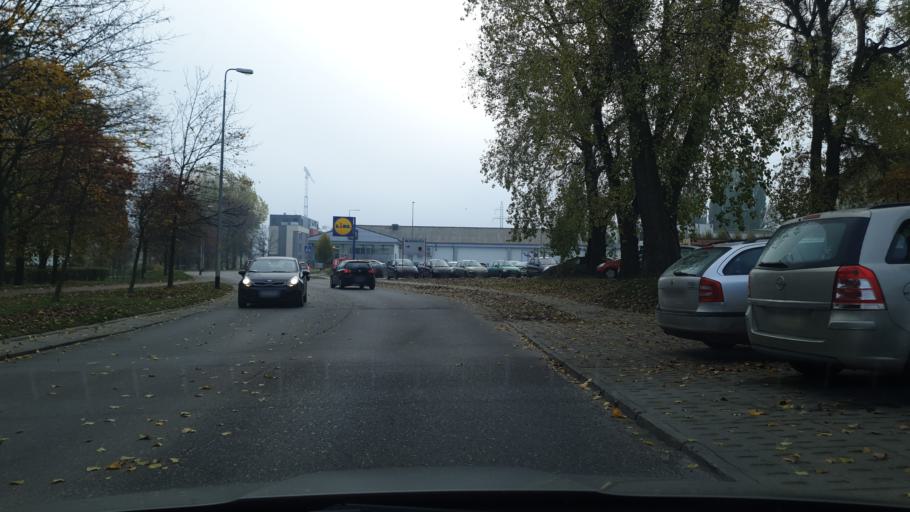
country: PL
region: Pomeranian Voivodeship
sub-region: Sopot
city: Sopot
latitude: 54.3916
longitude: 18.5905
